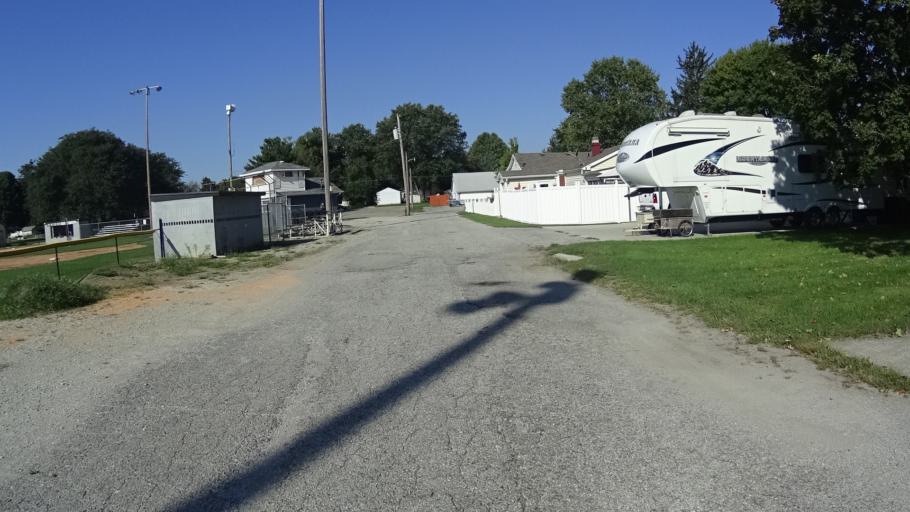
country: US
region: Indiana
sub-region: Madison County
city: Lapel
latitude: 40.0639
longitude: -85.8473
